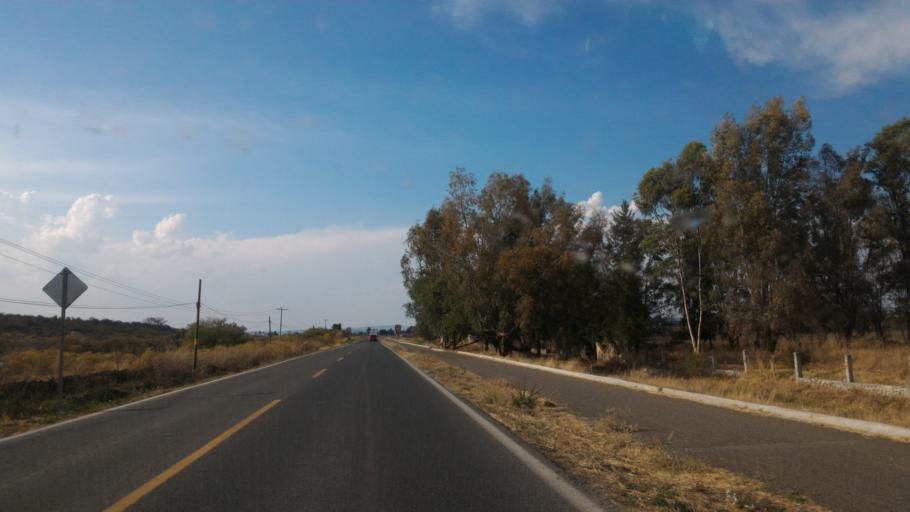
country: MX
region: Guanajuato
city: Ciudad Manuel Doblado
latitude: 20.7487
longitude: -101.9611
